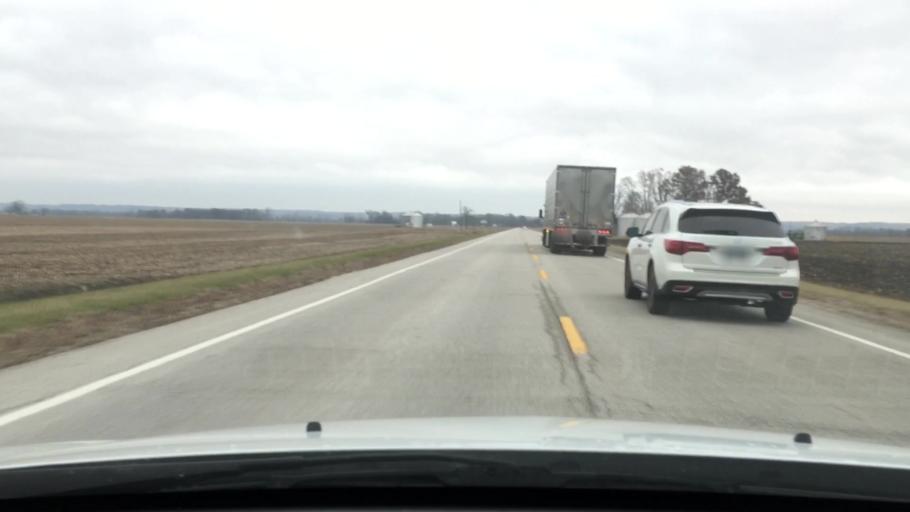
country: US
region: Missouri
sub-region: Pike County
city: Louisiana
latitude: 39.4745
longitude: -91.0219
